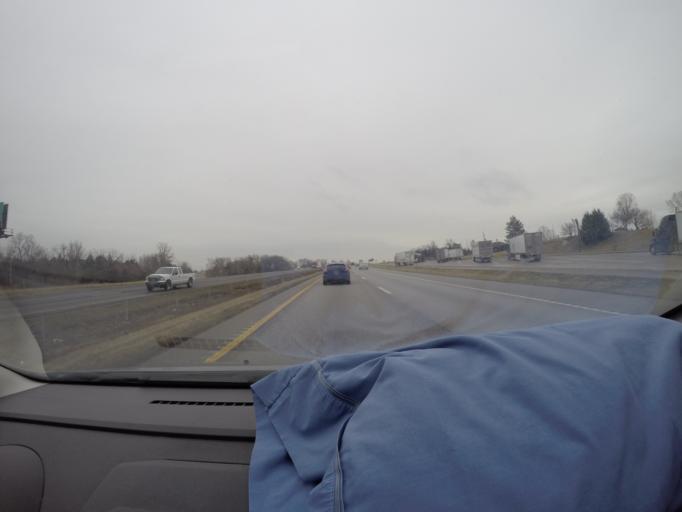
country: US
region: Missouri
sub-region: Warren County
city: Wright City
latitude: 38.8274
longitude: -91.0559
